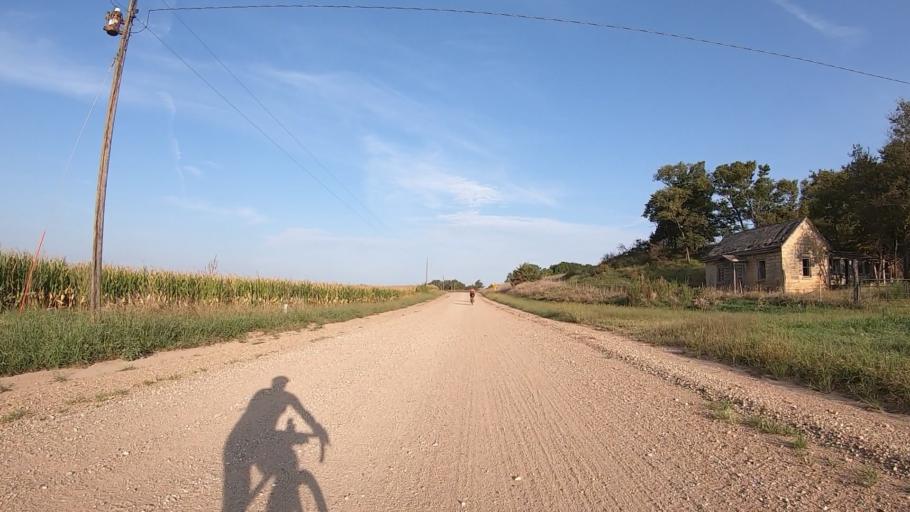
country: US
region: Kansas
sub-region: Marshall County
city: Blue Rapids
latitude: 39.7252
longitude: -96.7847
